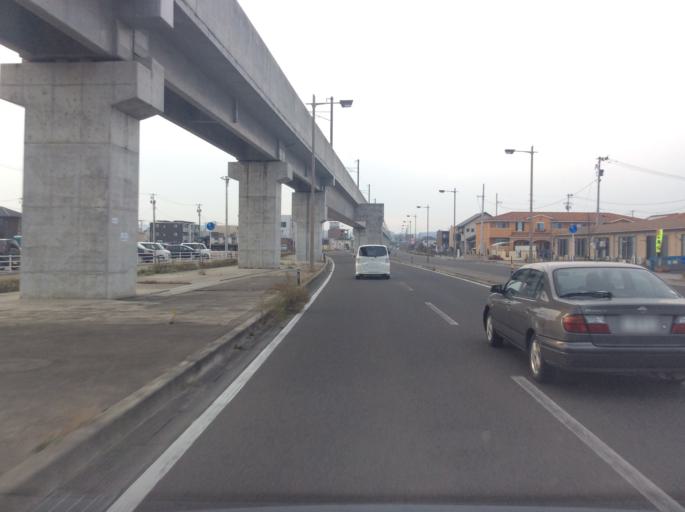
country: JP
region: Miyagi
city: Iwanuma
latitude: 38.1605
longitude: 140.9149
